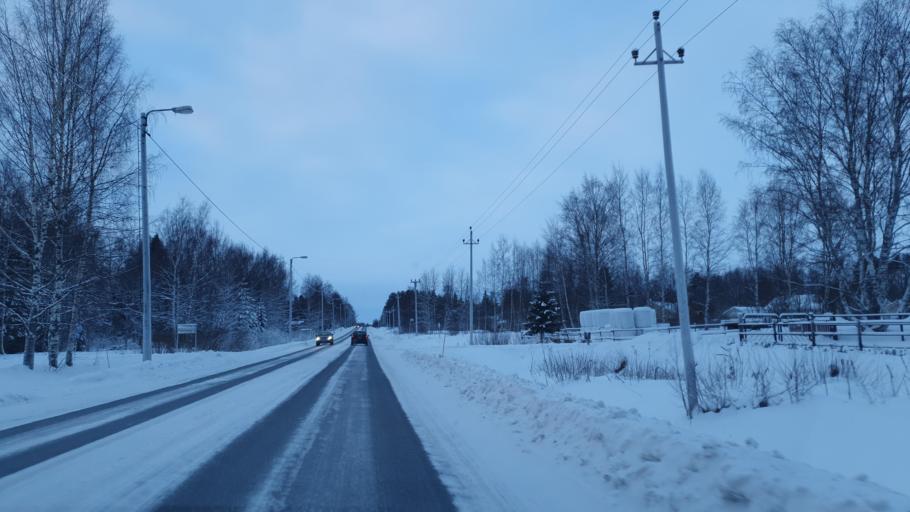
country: FI
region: Northern Ostrobothnia
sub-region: Oulu
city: Haukipudas
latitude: 65.1969
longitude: 25.3851
